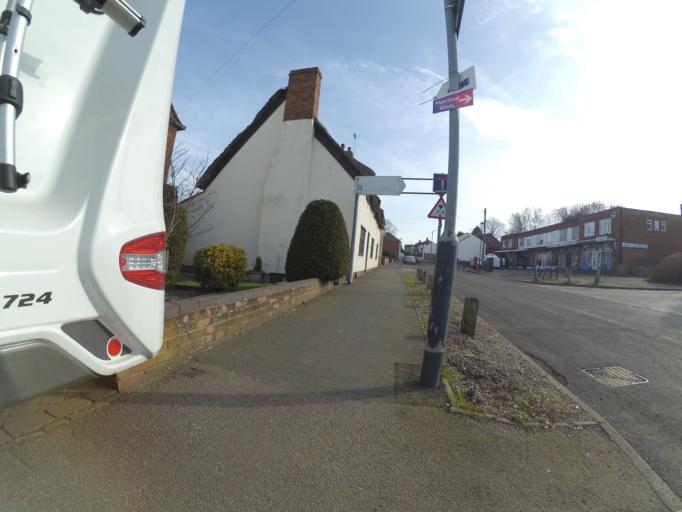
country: GB
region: England
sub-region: Warwickshire
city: Rugby
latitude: 52.3612
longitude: -1.2127
